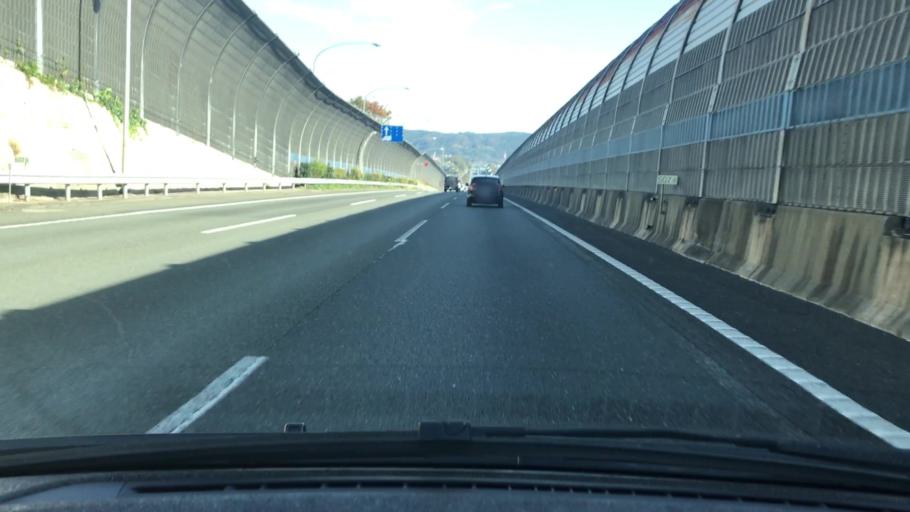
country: JP
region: Osaka
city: Takatsuki
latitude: 34.8557
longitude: 135.5912
